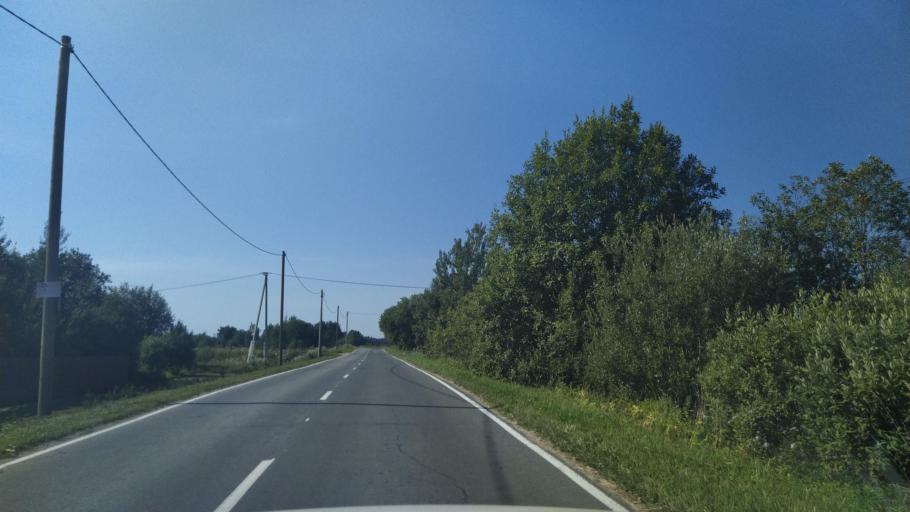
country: RU
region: Leningrad
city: Siverskiy
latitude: 59.2881
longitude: 30.0596
